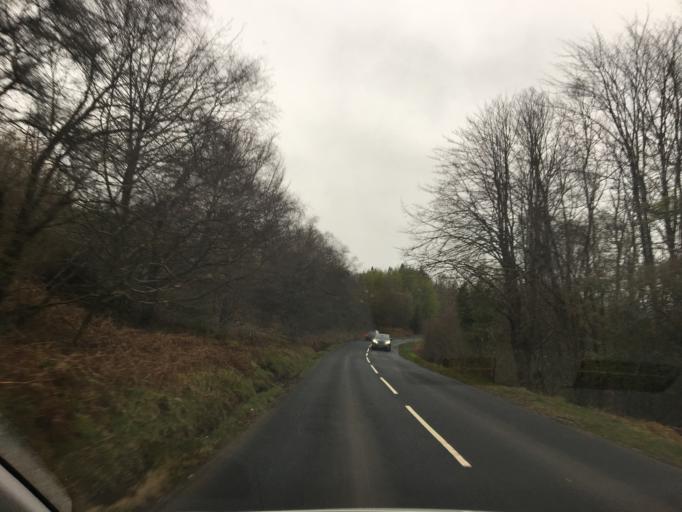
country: GB
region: Scotland
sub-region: North Ayrshire
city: Lamlash
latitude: 55.5498
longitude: -5.1402
